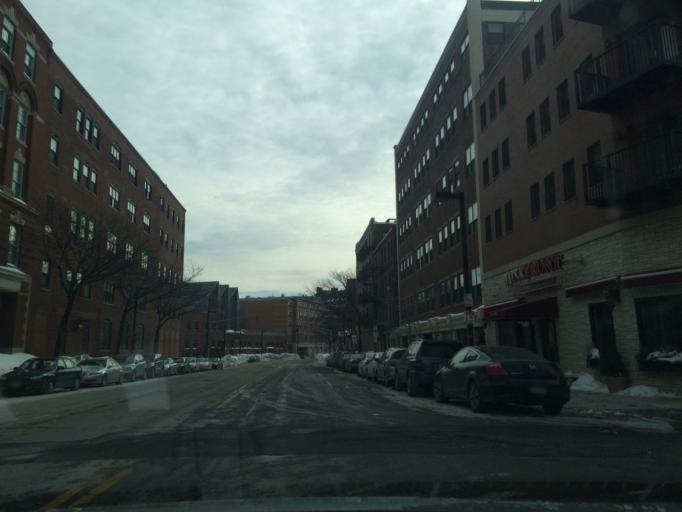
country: US
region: Massachusetts
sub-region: Suffolk County
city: Boston
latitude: 42.3675
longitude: -71.0536
